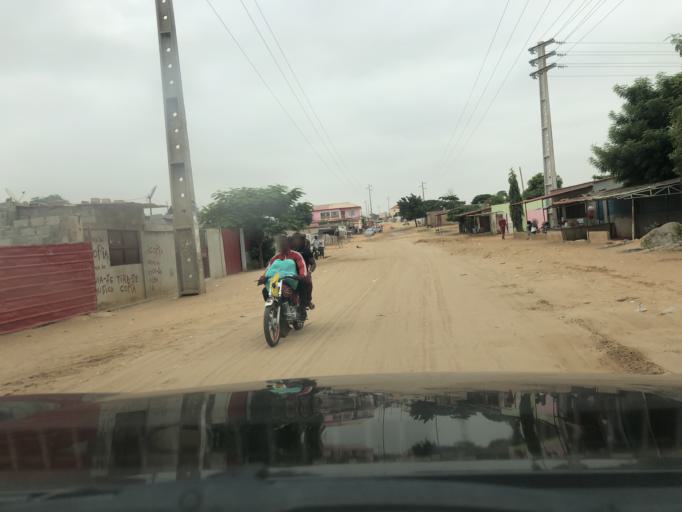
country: AO
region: Luanda
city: Luanda
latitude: -8.9397
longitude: 13.2393
